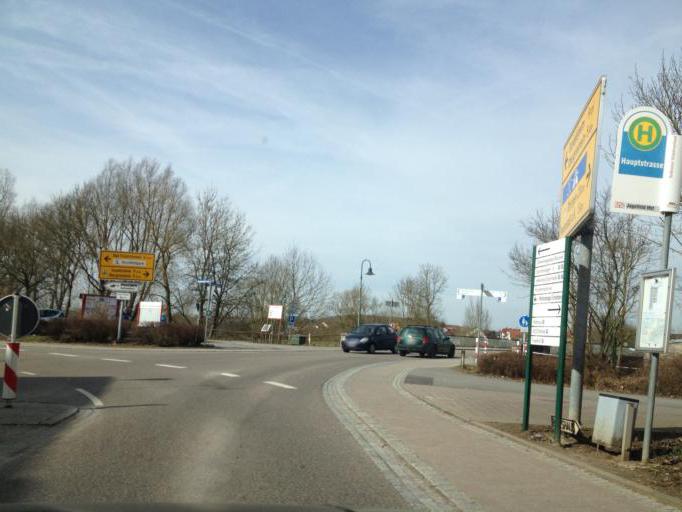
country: DE
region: Baden-Wuerttemberg
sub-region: Regierungsbezirk Stuttgart
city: Oedheim
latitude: 49.2391
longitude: 9.2518
